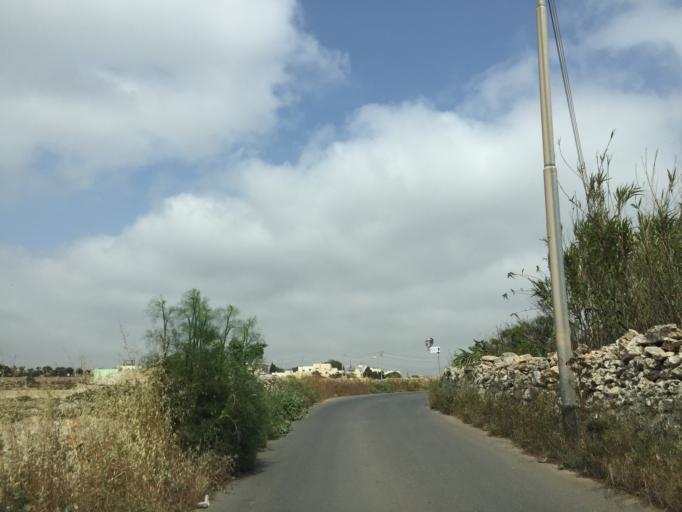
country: MT
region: L-Imgarr
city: Imgarr
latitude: 35.8972
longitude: 14.3632
